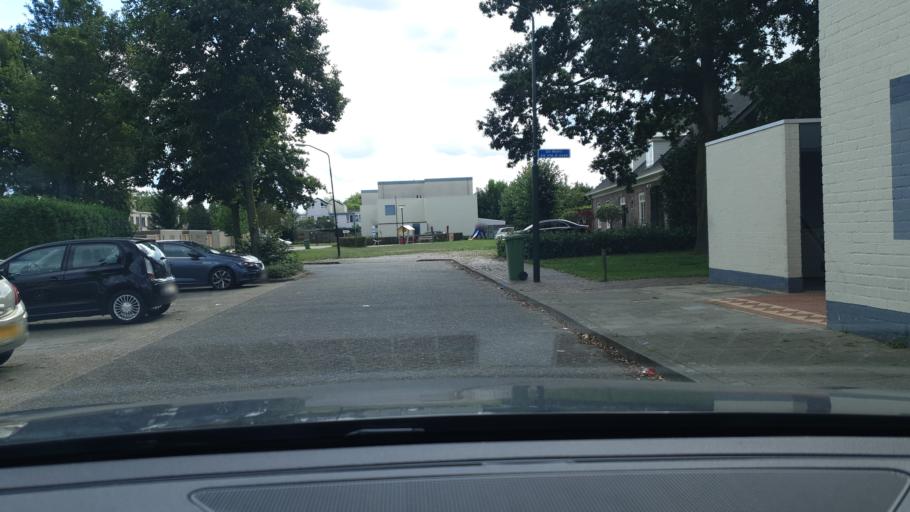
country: NL
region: North Brabant
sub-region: Gemeente Veghel
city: Veghel
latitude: 51.6085
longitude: 5.5383
